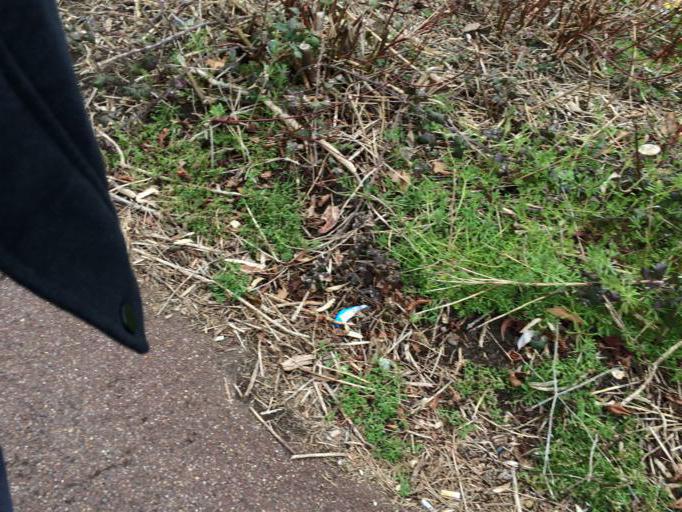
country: GB
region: England
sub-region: Milton Keynes
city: Milton Keynes
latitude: 52.0348
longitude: -0.7697
